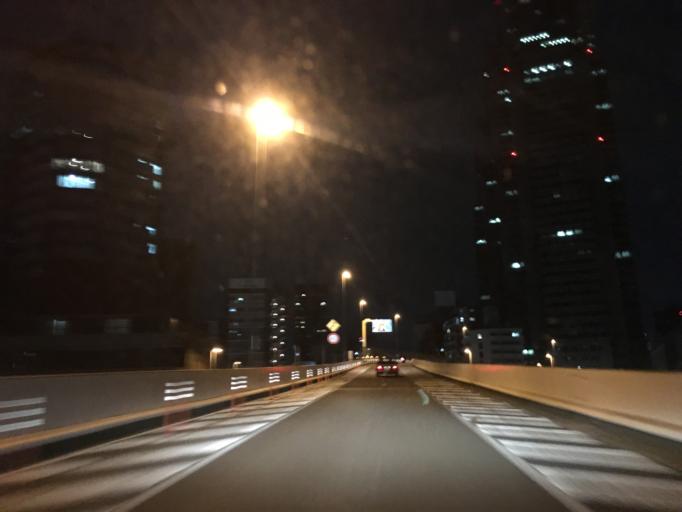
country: JP
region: Tokyo
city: Tokyo
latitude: 35.6828
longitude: 139.6916
